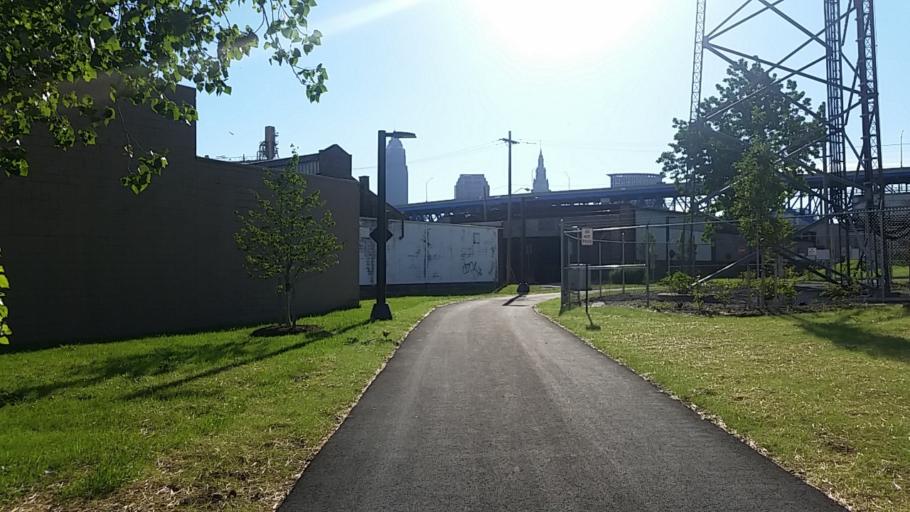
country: US
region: Ohio
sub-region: Cuyahoga County
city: Cleveland
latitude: 41.4954
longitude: -81.7106
